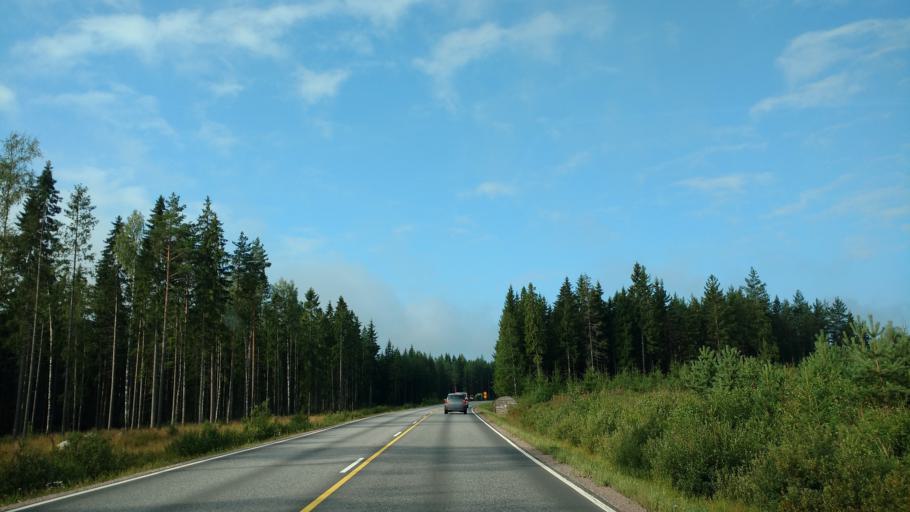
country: FI
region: Varsinais-Suomi
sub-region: Aboland-Turunmaa
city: Vaestanfjaerd
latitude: 60.1191
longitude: 22.6226
